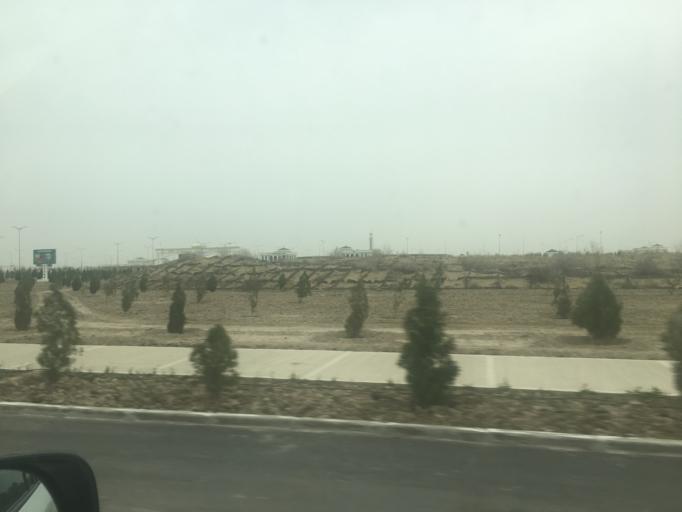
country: TM
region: Lebap
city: Turkmenabat
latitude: 38.9724
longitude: 63.5079
